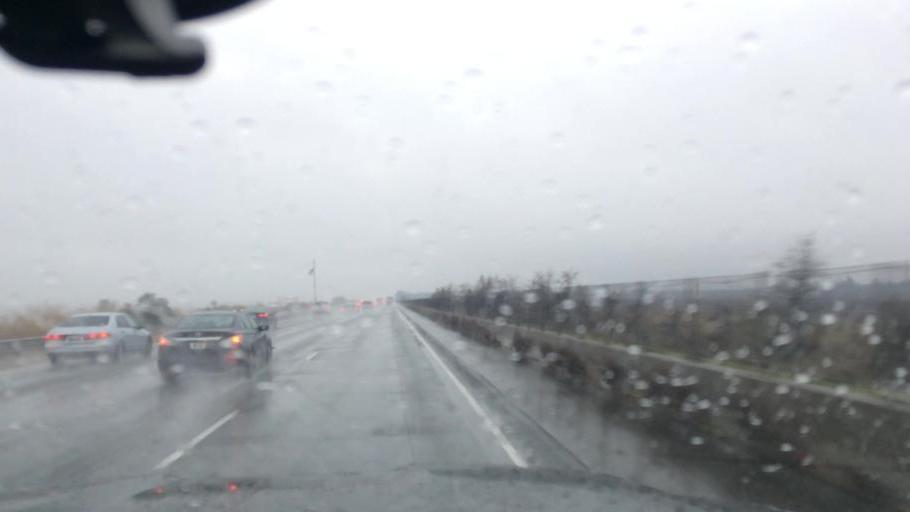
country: US
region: California
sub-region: Yolo County
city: West Sacramento
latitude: 38.5677
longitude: -121.6160
